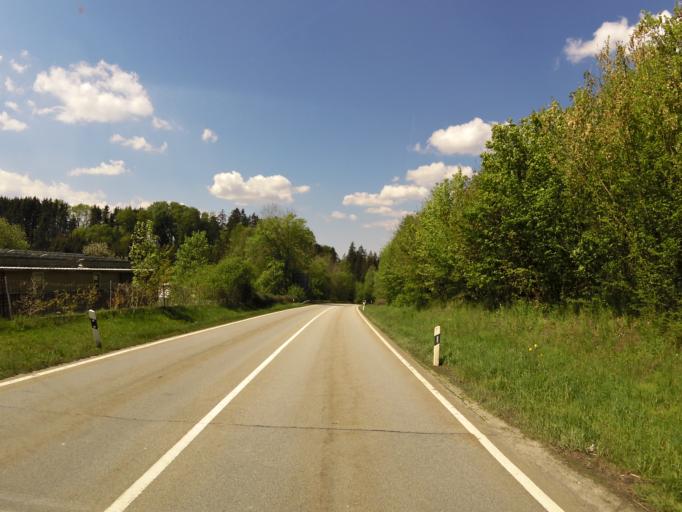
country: DE
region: Bavaria
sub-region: Lower Bavaria
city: Hutthurm
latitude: 48.6783
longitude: 13.4818
